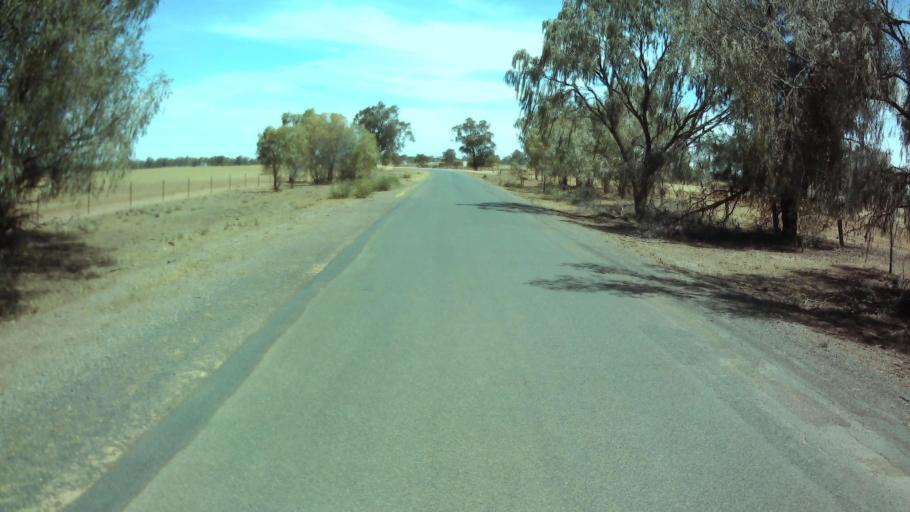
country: AU
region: New South Wales
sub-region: Weddin
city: Grenfell
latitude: -33.8297
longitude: 147.7459
